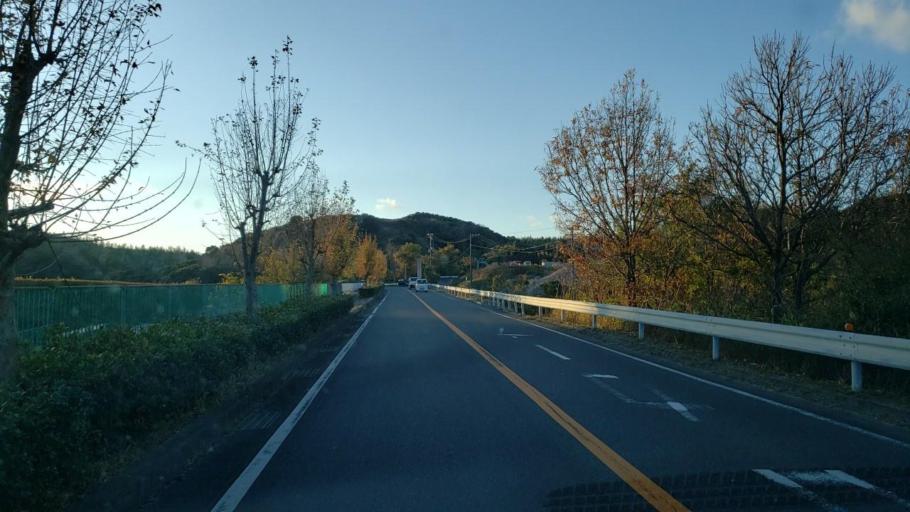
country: JP
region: Hyogo
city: Sumoto
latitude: 34.4423
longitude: 134.9084
